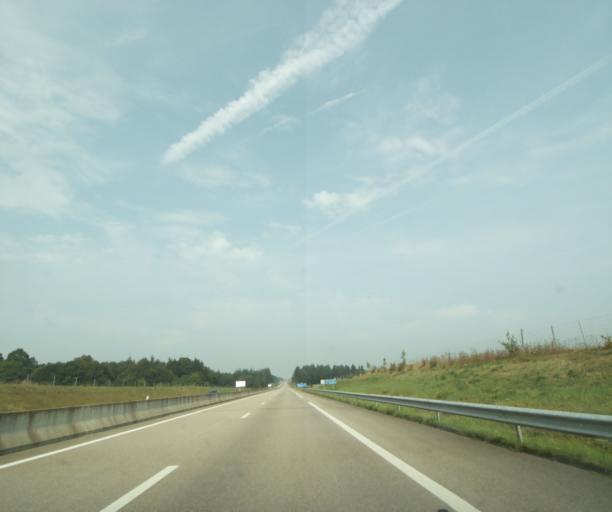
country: FR
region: Lower Normandy
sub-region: Departement de l'Orne
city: Courteilles
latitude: 48.8297
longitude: -0.1437
